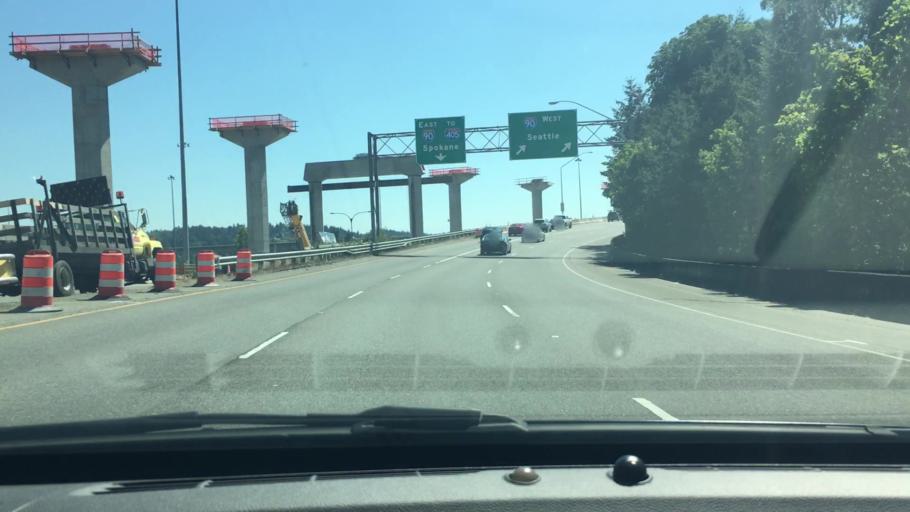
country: US
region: Washington
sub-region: King County
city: Newport
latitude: 47.5821
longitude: -122.1881
